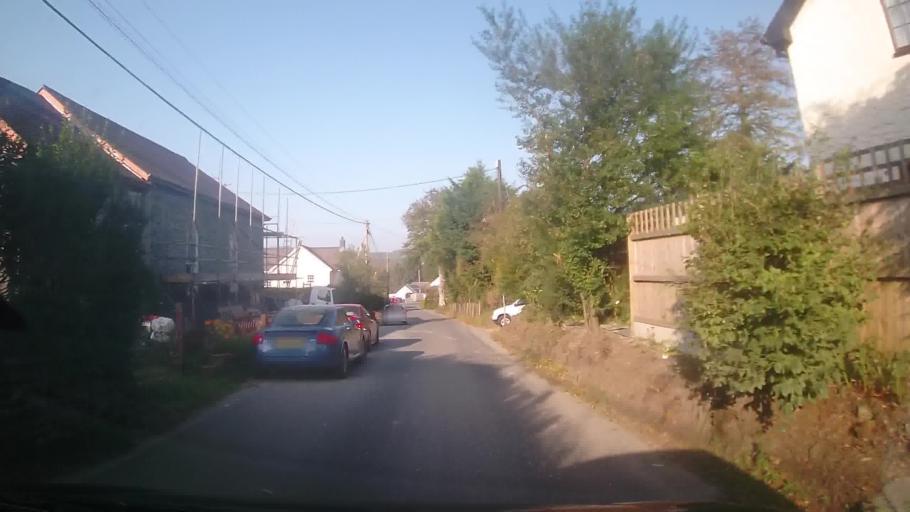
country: GB
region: Wales
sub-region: County of Ceredigion
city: Lledrod
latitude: 52.3747
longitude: -3.8576
